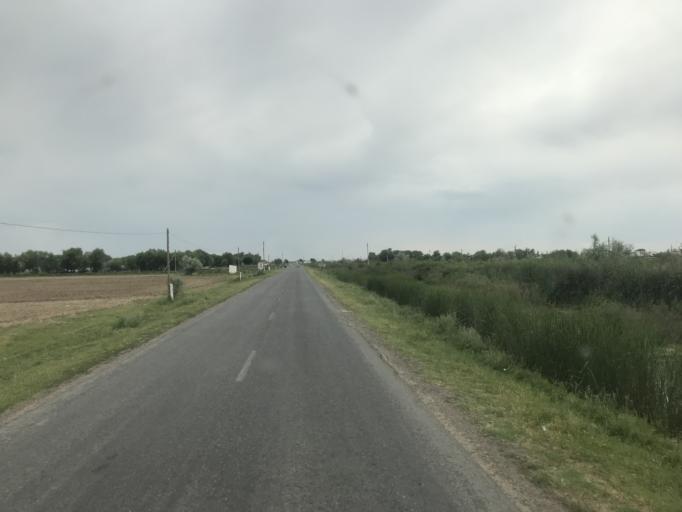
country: KZ
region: Ongtustik Qazaqstan
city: Asykata
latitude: 40.9169
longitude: 68.3970
